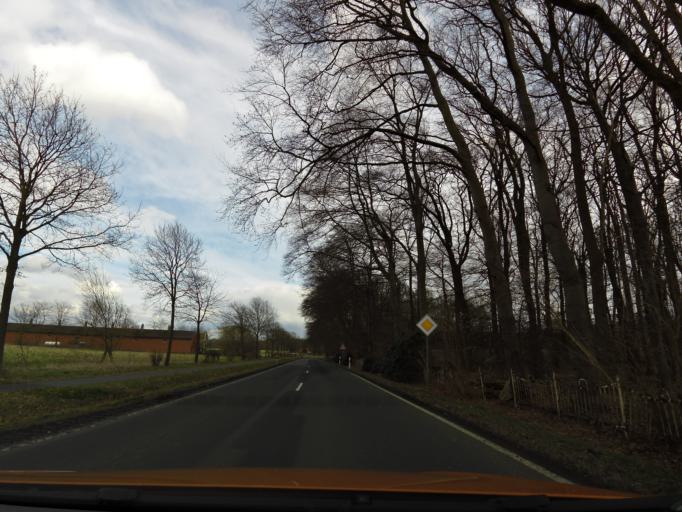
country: DE
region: Lower Saxony
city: Wildeshausen
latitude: 52.9337
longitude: 8.4783
